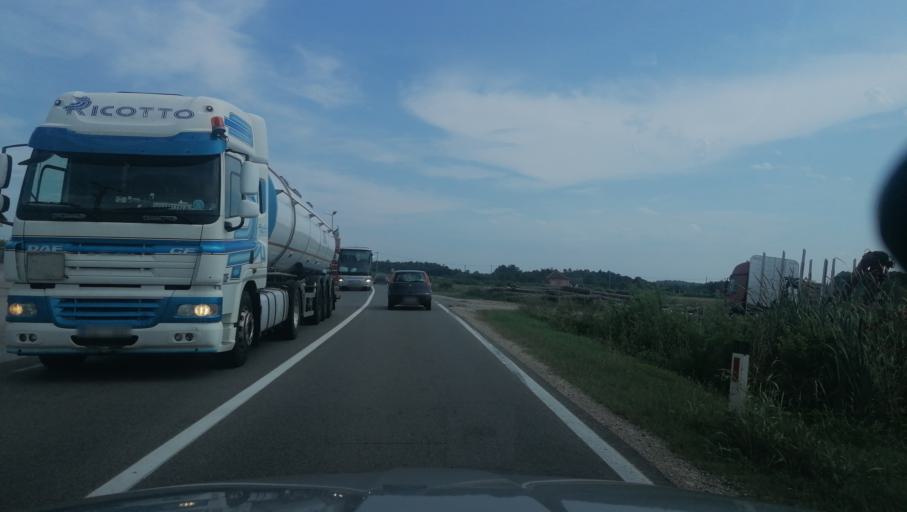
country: HR
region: Vukovarsko-Srijemska
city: Soljani
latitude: 44.8323
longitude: 18.9896
